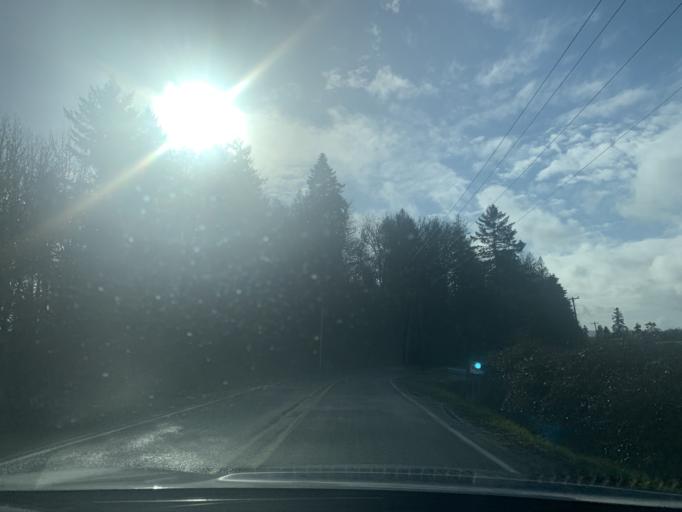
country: US
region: Oregon
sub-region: Washington County
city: King City
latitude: 45.3979
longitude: -122.8417
